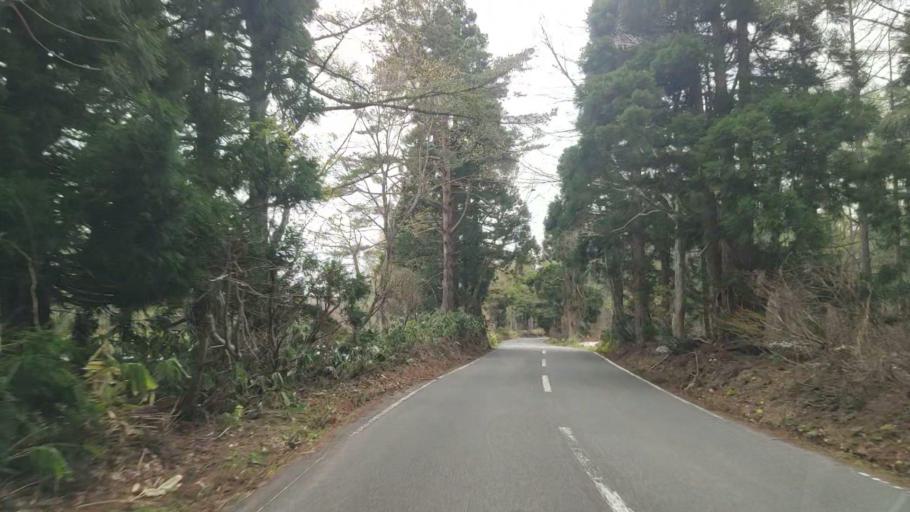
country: JP
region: Aomori
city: Aomori Shi
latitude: 40.7224
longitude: 140.8562
